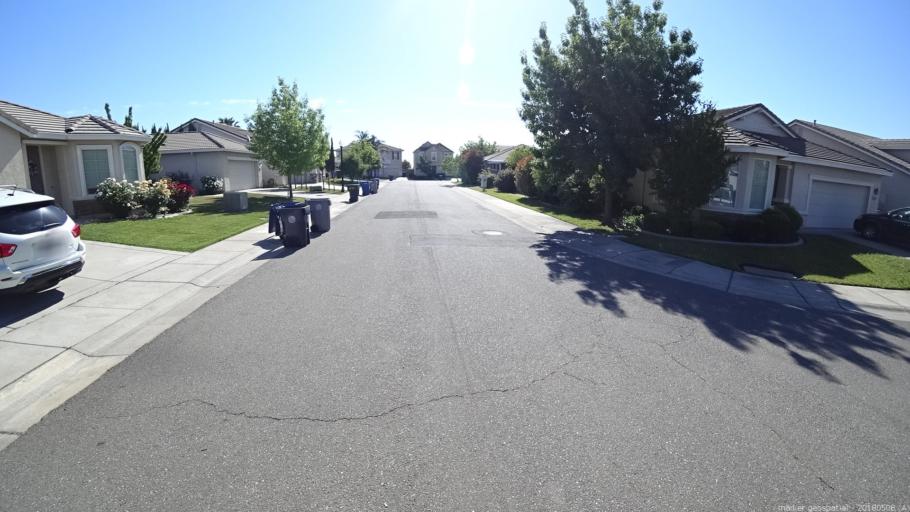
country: US
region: California
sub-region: Sacramento County
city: Elverta
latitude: 38.6841
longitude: -121.4949
